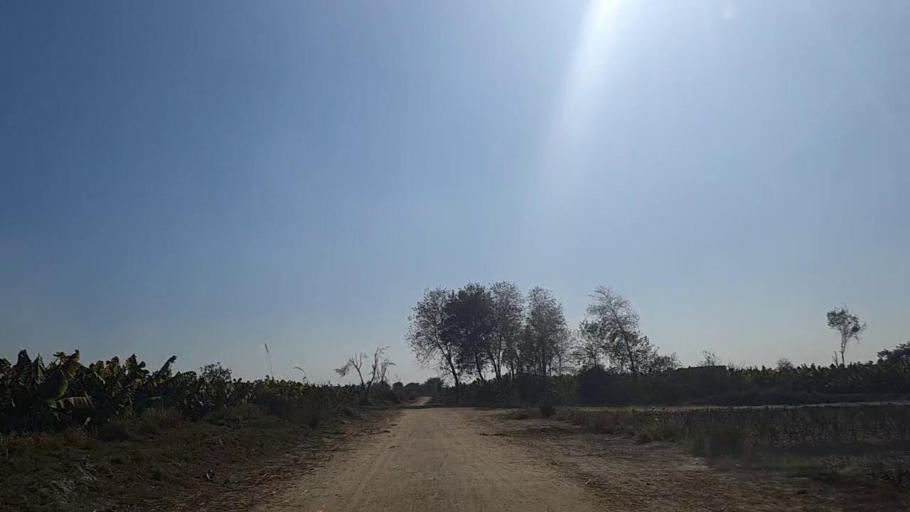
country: PK
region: Sindh
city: Sakrand
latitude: 26.2395
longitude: 68.1998
